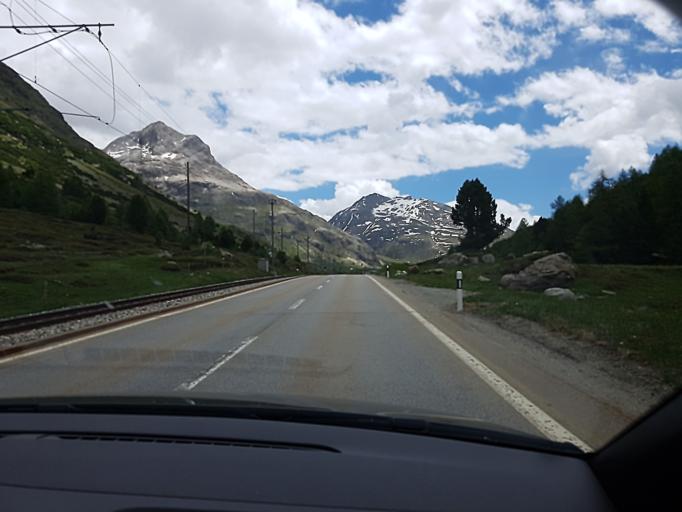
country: CH
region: Grisons
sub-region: Maloja District
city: Pontresina
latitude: 46.4485
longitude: 9.9585
